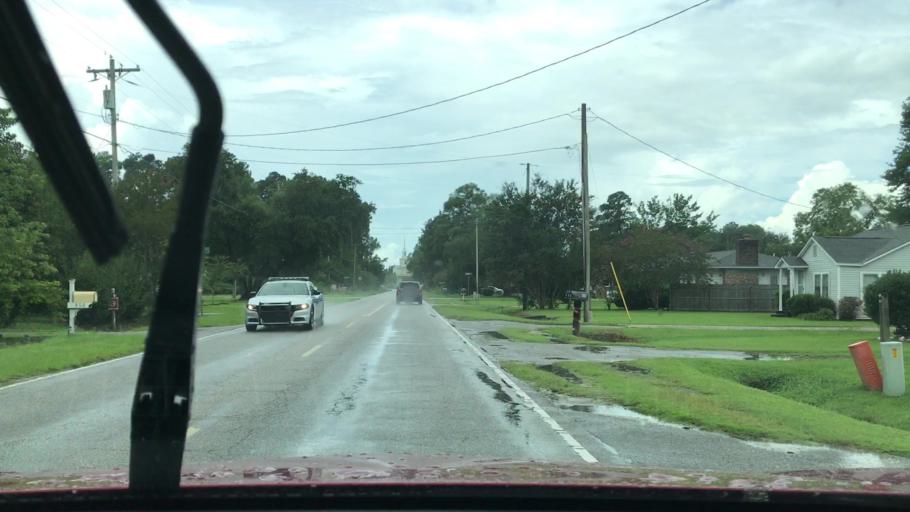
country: US
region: South Carolina
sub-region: Horry County
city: Red Hill
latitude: 33.8499
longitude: -79.0190
